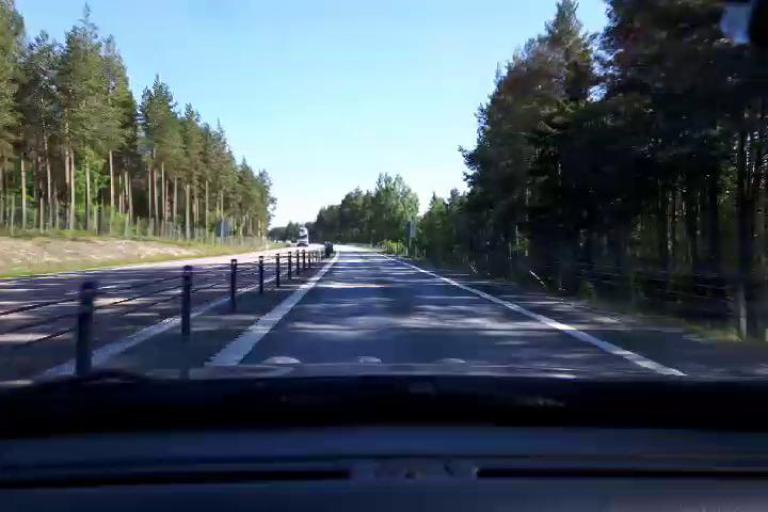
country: SE
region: Gaevleborg
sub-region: Gavle Kommun
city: Norrsundet
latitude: 60.9975
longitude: 16.9944
